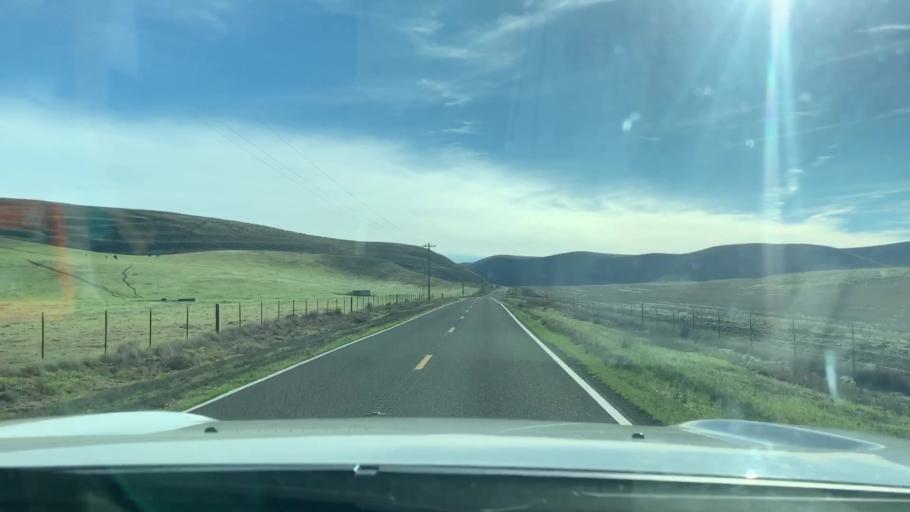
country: US
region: California
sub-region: Monterey County
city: King City
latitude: 36.1561
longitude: -120.9777
